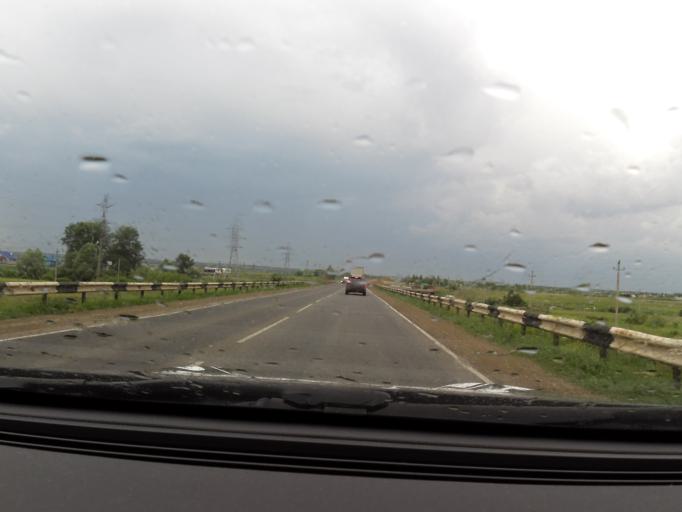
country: RU
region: Bashkortostan
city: Asanovo
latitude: 54.9041
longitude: 55.6223
